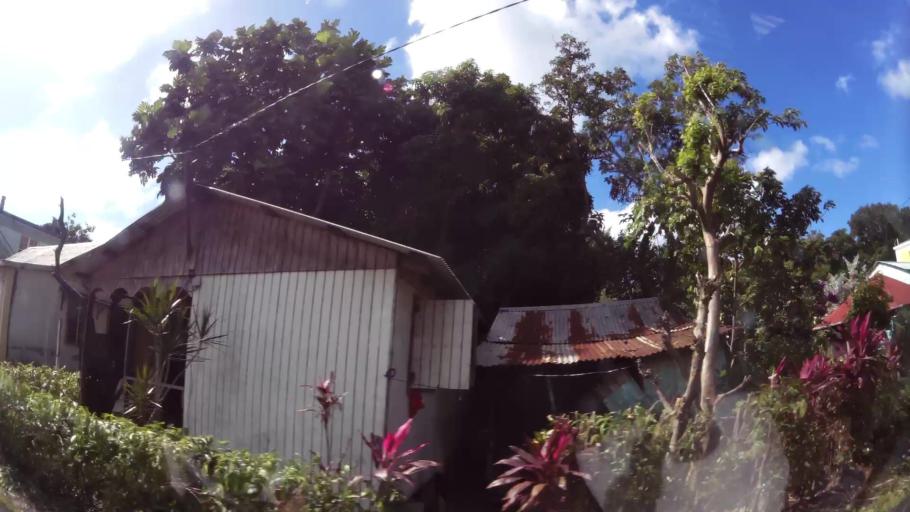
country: DM
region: Saint John
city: Portsmouth
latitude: 15.5835
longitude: -61.4612
